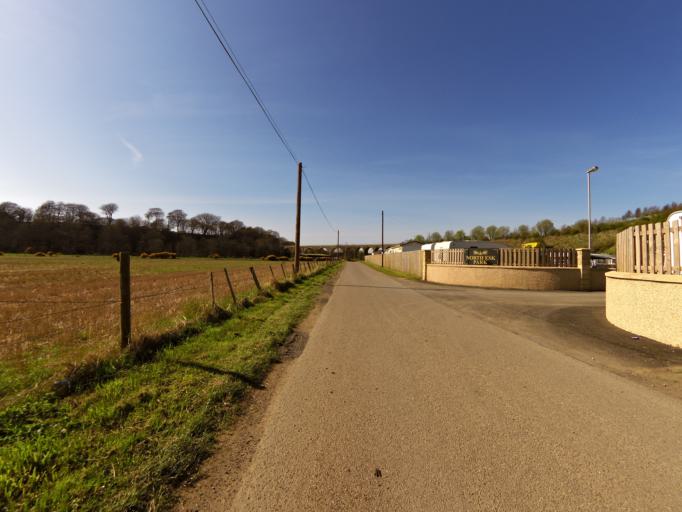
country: GB
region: Scotland
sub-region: Angus
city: Montrose
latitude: 56.7535
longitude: -2.4483
